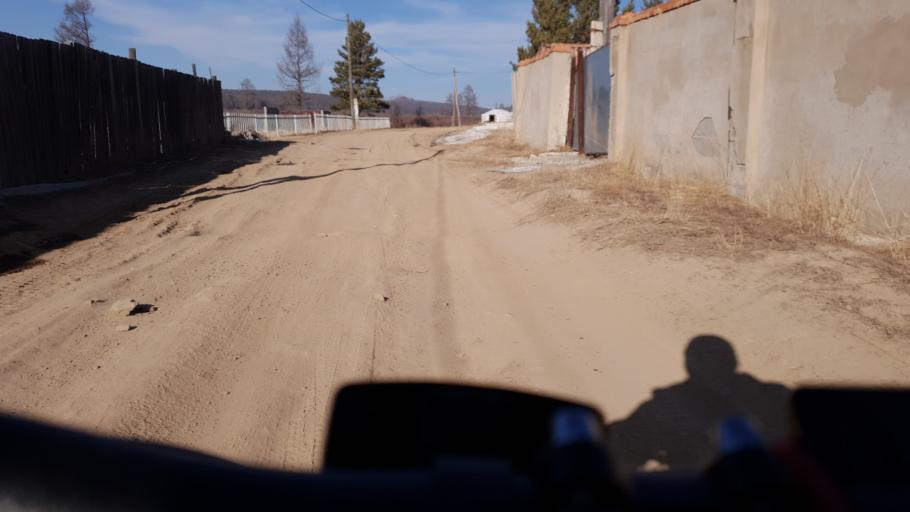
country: MN
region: Ulaanbaatar
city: Ulaanbaatar
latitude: 48.1563
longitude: 106.8814
